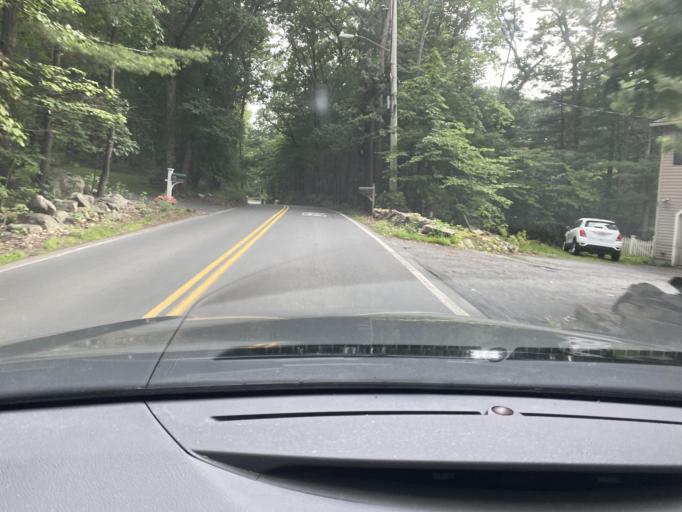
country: US
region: Massachusetts
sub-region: Norfolk County
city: Walpole
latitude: 42.1794
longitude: -71.2508
